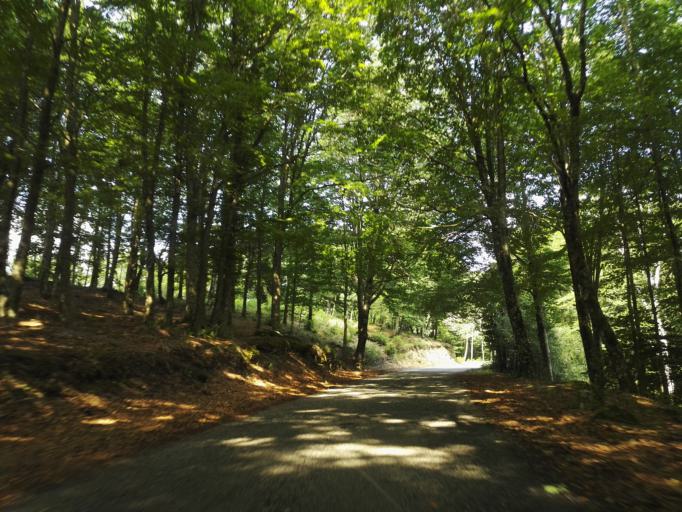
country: IT
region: Calabria
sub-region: Provincia di Vibo-Valentia
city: Nardodipace
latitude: 38.5002
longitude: 16.3838
